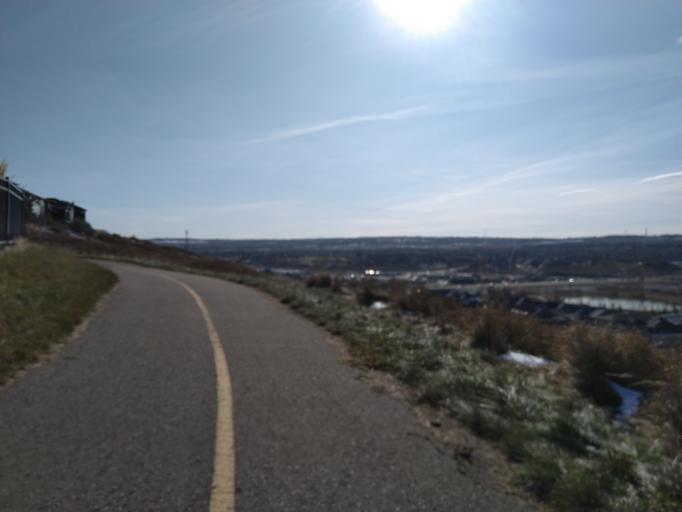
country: CA
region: Alberta
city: Calgary
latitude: 51.1726
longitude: -114.1240
